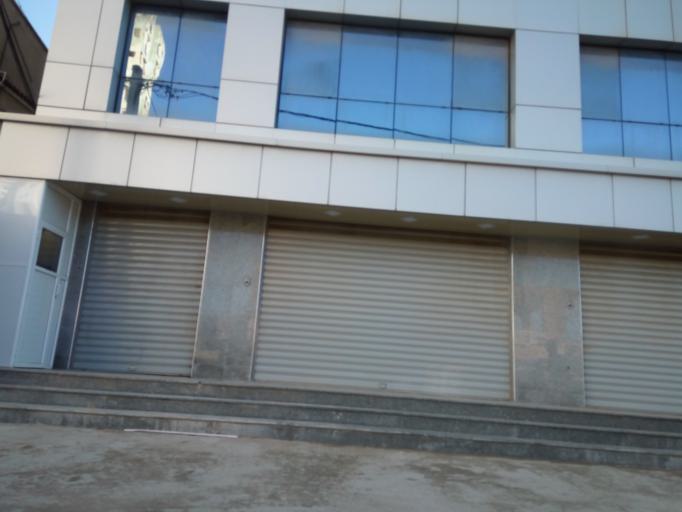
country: DZ
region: Tipaza
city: Saoula
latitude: 36.7301
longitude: 3.0023
